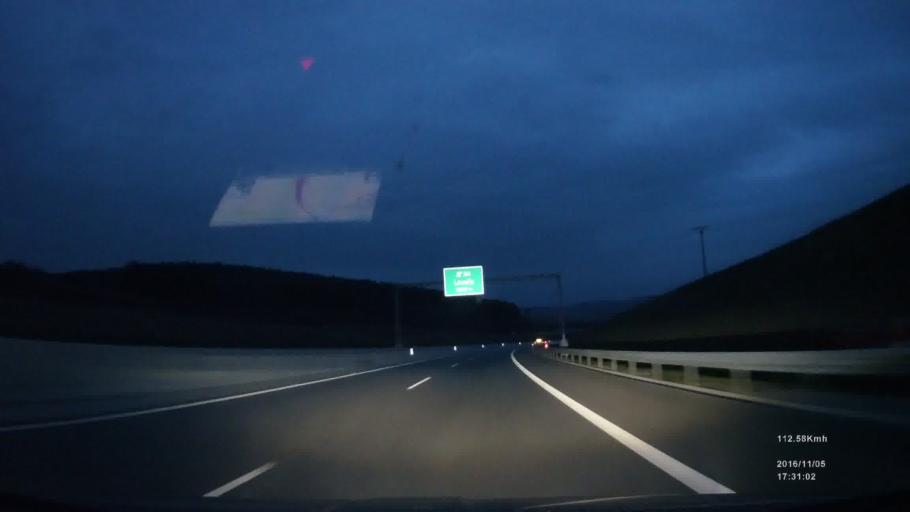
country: SK
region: Presovsky
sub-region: Okres Presov
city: Levoca
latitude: 49.0022
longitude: 20.5392
